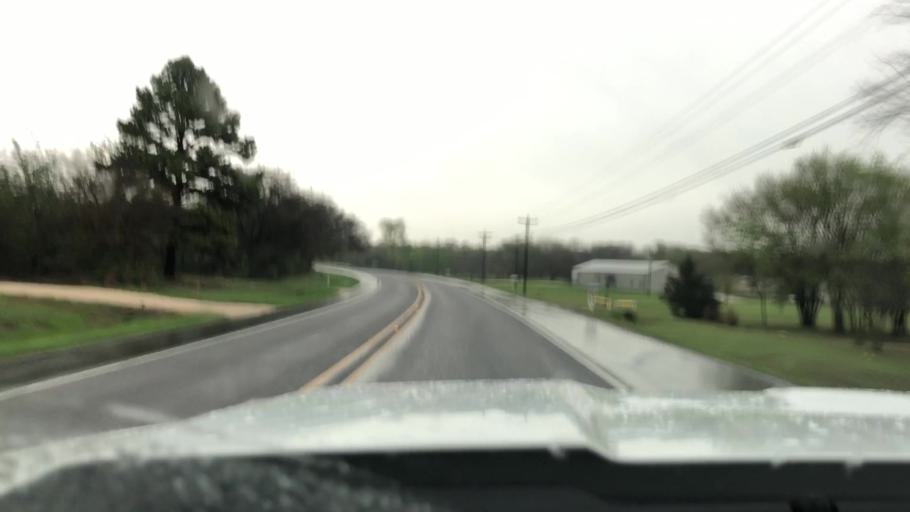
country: US
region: Texas
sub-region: Johnson County
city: Keene
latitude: 32.4348
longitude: -97.3118
